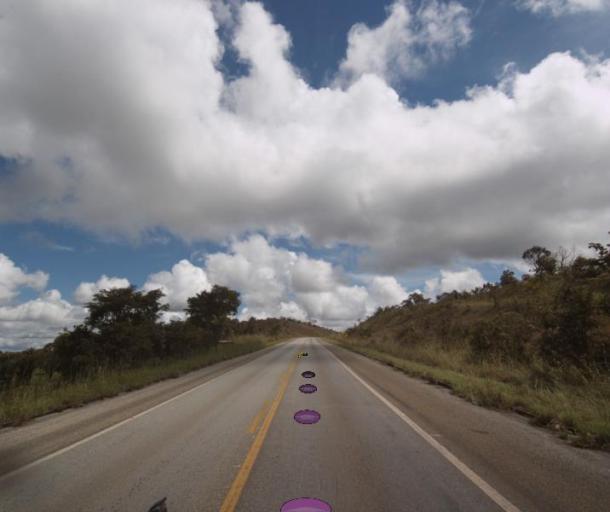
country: BR
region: Goias
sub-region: Pirenopolis
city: Pirenopolis
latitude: -15.7721
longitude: -48.5524
